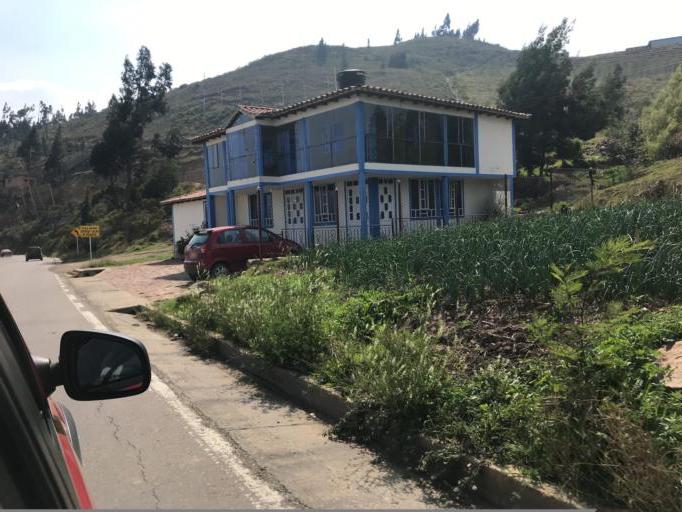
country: CO
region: Boyaca
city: Cucaita
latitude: 5.5457
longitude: -73.4922
